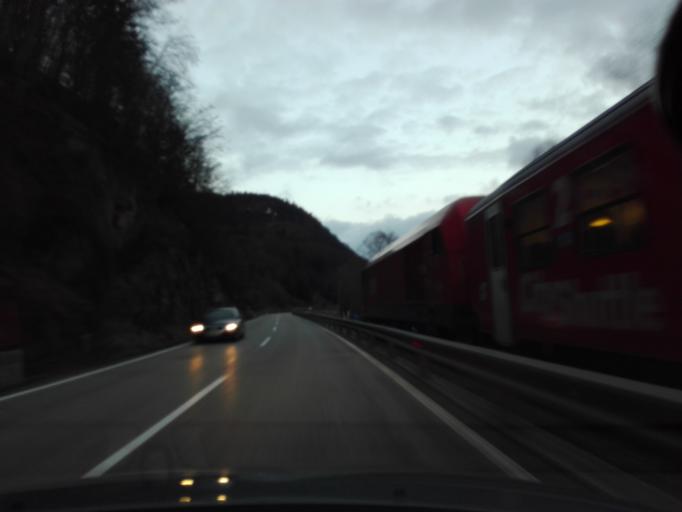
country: AT
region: Upper Austria
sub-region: Politischer Bezirk Perg
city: Bad Kreuzen
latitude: 48.2010
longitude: 14.8457
